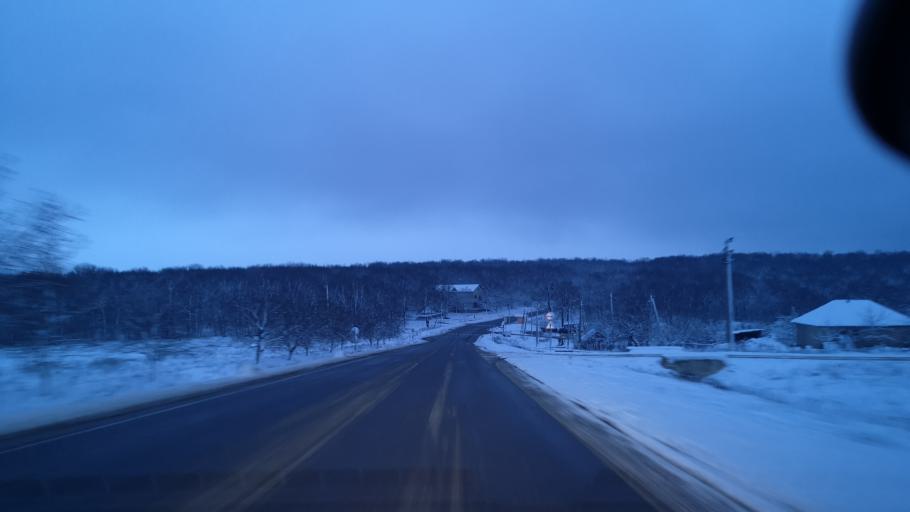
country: MD
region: Rezina
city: Rezina
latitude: 47.7342
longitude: 28.8771
